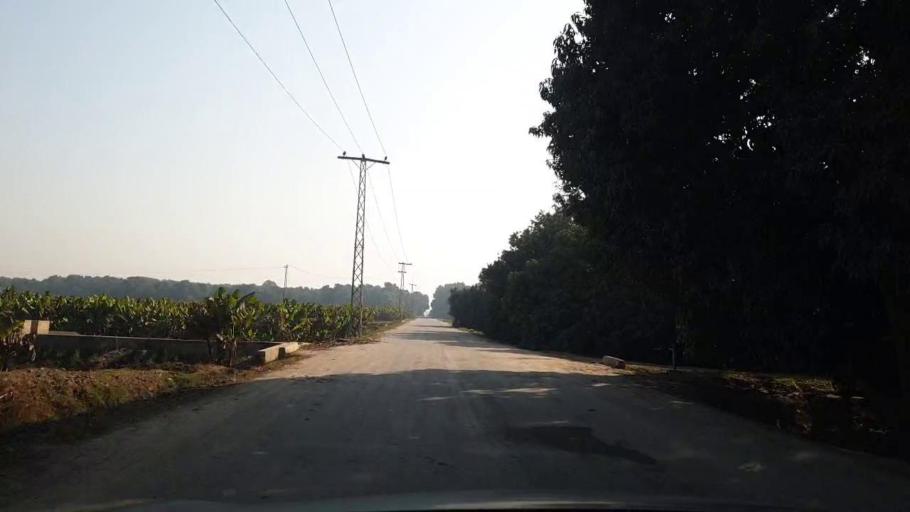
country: PK
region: Sindh
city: Tando Allahyar
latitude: 25.5094
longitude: 68.7178
